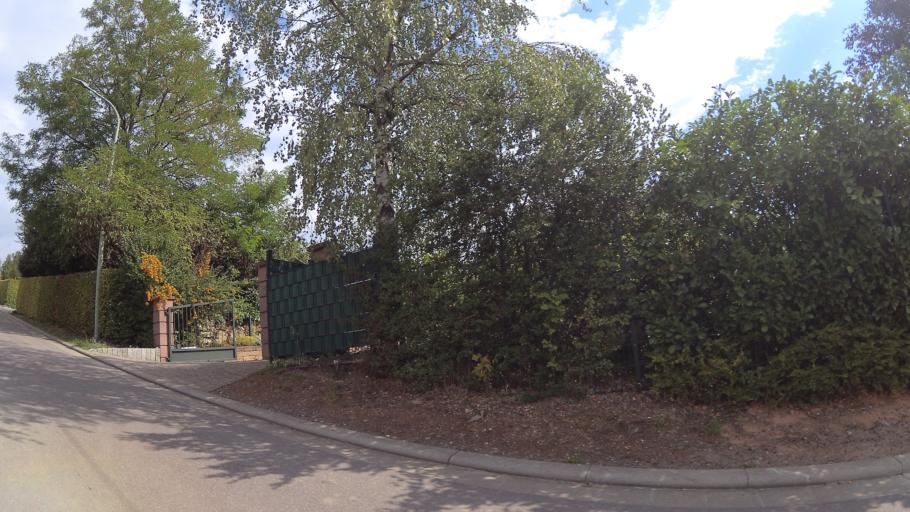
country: DE
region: Saarland
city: Gersheim
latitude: 49.1411
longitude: 7.1805
